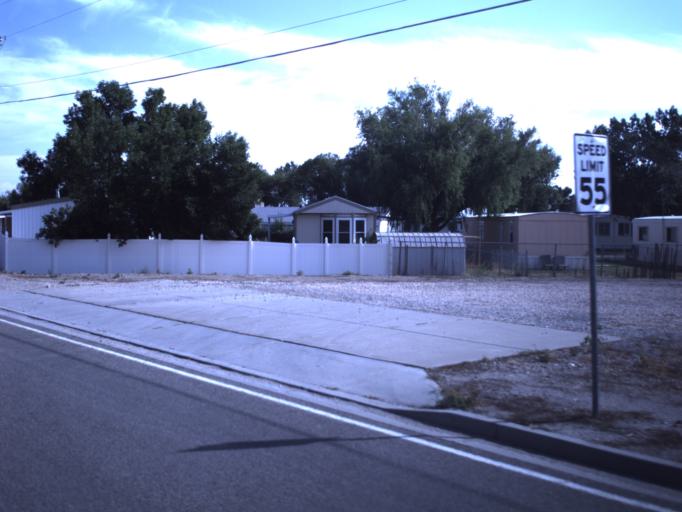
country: US
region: Utah
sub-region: Weber County
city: Pleasant View
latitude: 41.3035
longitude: -112.0027
